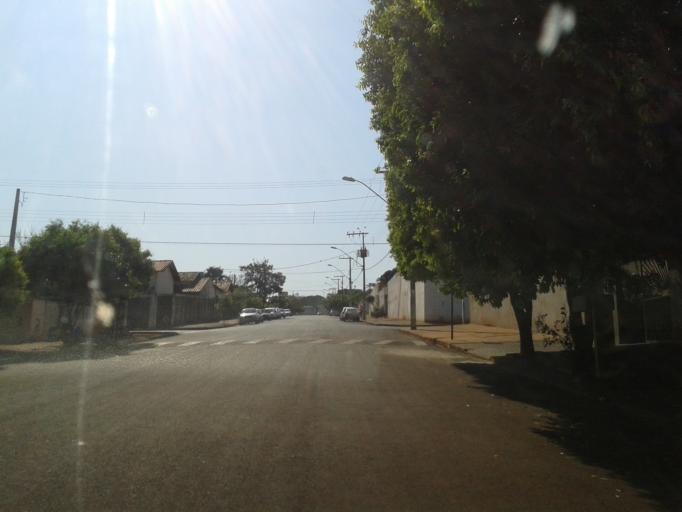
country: BR
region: Minas Gerais
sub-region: Ituiutaba
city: Ituiutaba
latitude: -18.9643
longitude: -49.4723
